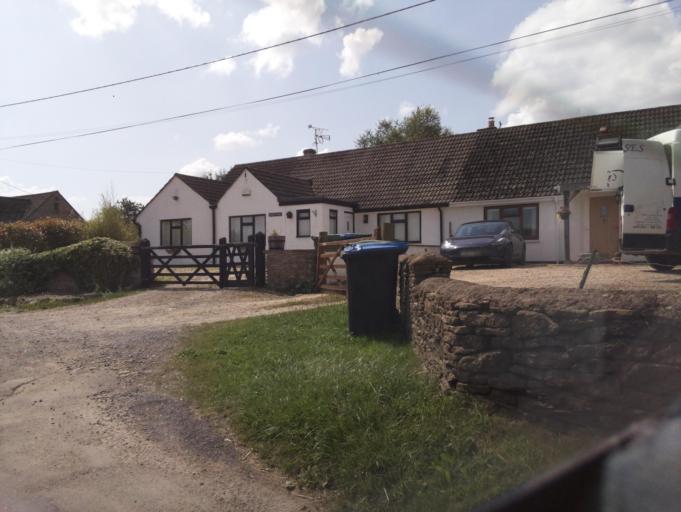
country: GB
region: England
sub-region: Wiltshire
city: Malmesbury
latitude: 51.5589
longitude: -2.1120
